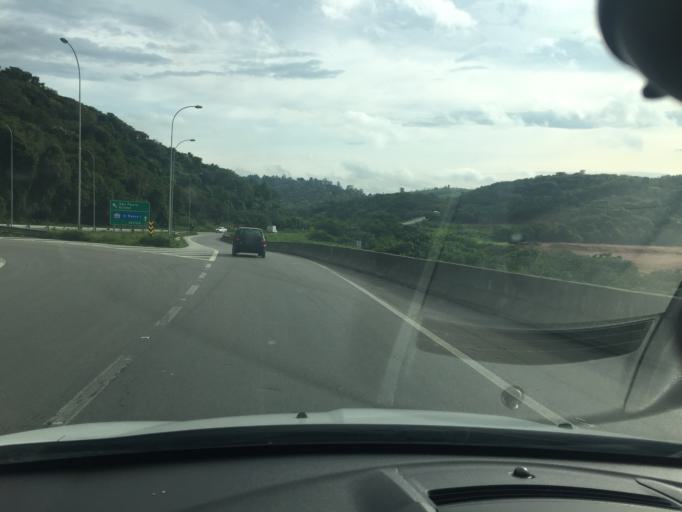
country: BR
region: Sao Paulo
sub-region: Campo Limpo Paulista
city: Campo Limpo Paulista
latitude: -23.1976
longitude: -46.7955
